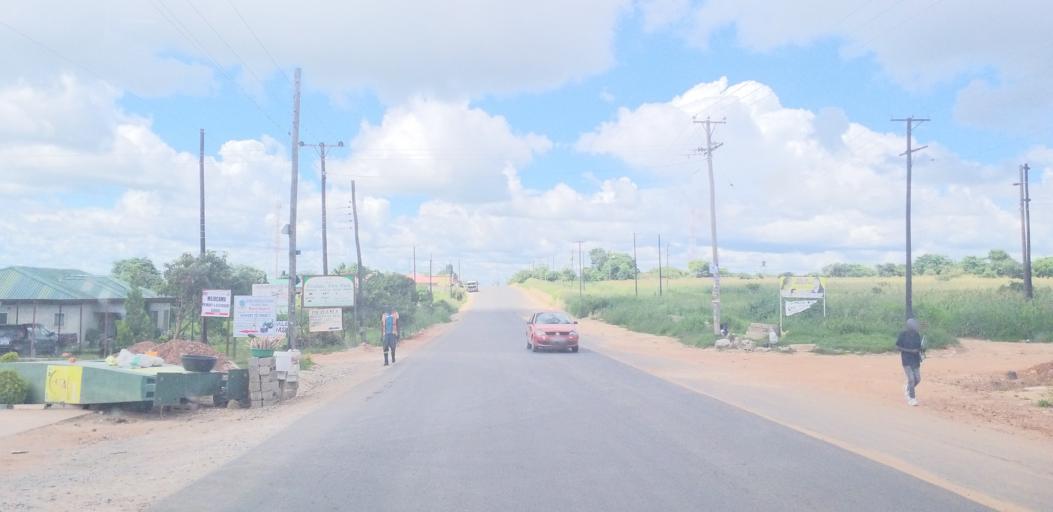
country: ZM
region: Lusaka
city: Lusaka
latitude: -15.3536
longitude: 28.3244
